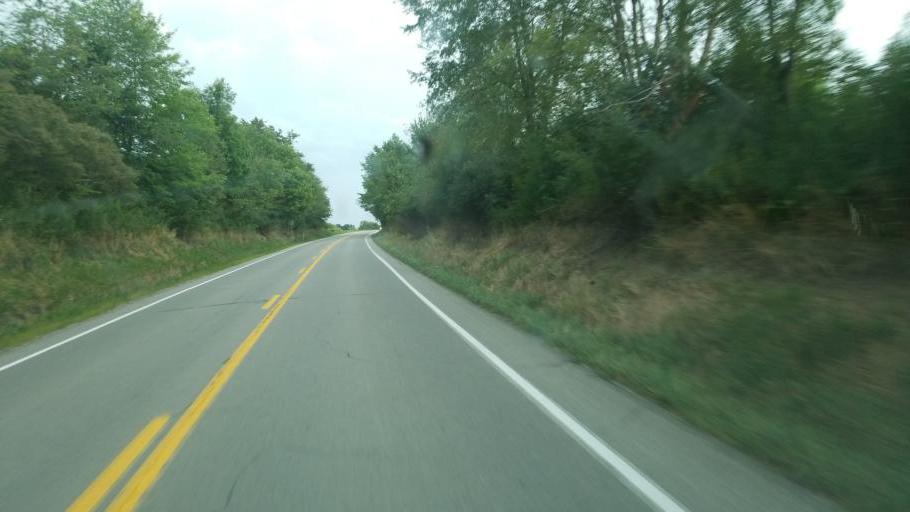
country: US
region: Pennsylvania
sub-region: Clarion County
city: Knox
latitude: 41.1985
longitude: -79.5445
